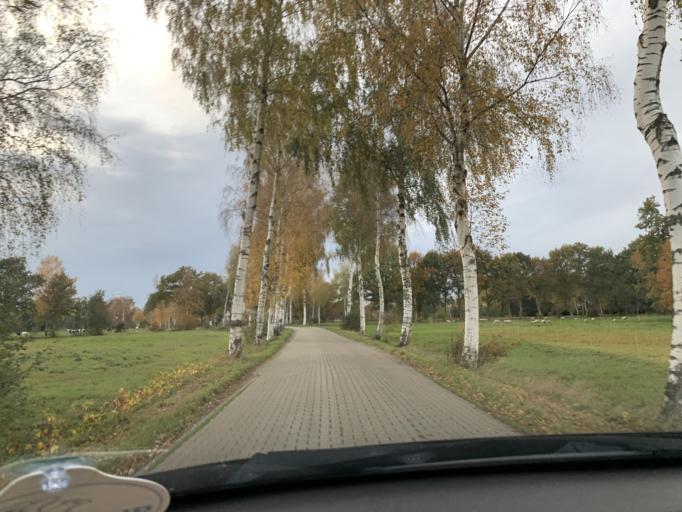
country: DE
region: Lower Saxony
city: Wiefelstede
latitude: 53.2656
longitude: 8.0620
